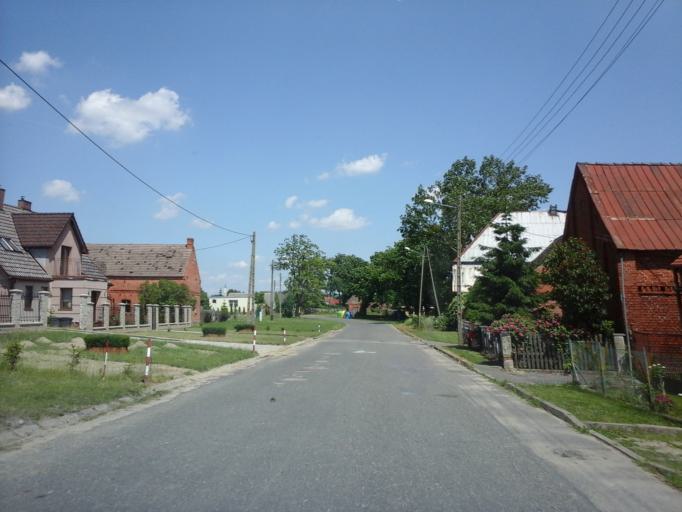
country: PL
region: West Pomeranian Voivodeship
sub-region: Powiat choszczenski
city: Choszczno
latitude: 53.1433
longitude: 15.3476
